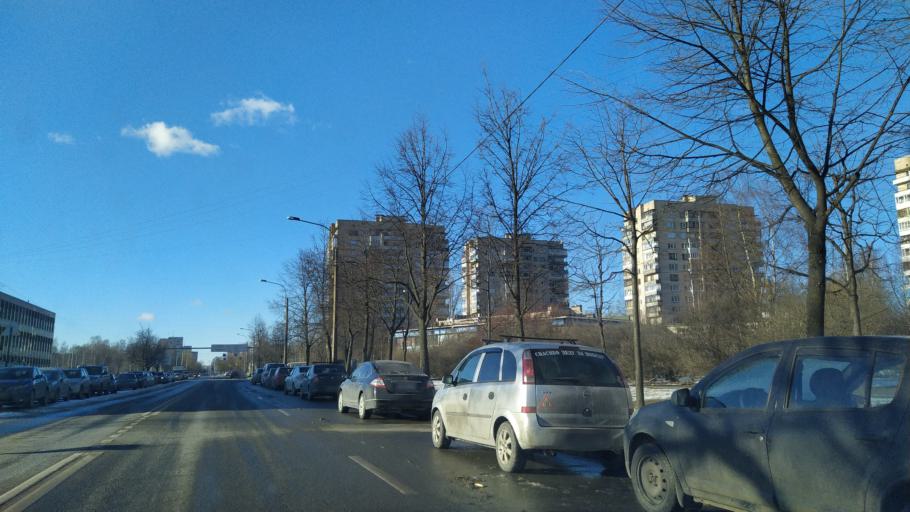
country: RU
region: Leningrad
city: Kalininskiy
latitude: 59.9723
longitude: 30.4188
